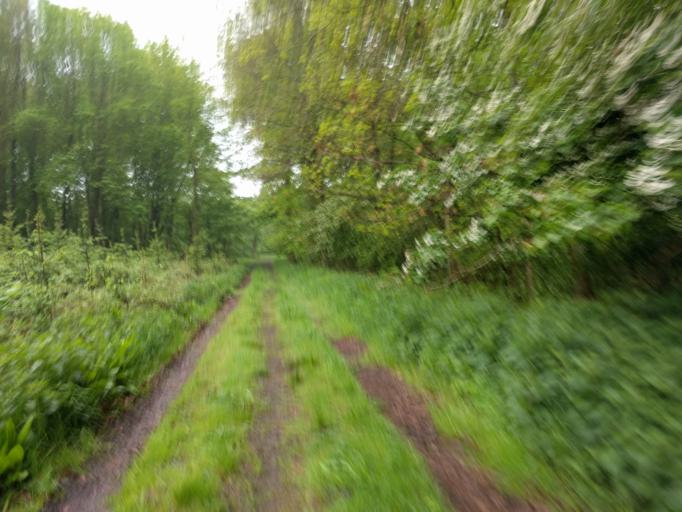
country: DK
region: South Denmark
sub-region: Kerteminde Kommune
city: Munkebo
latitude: 55.4327
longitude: 10.5523
